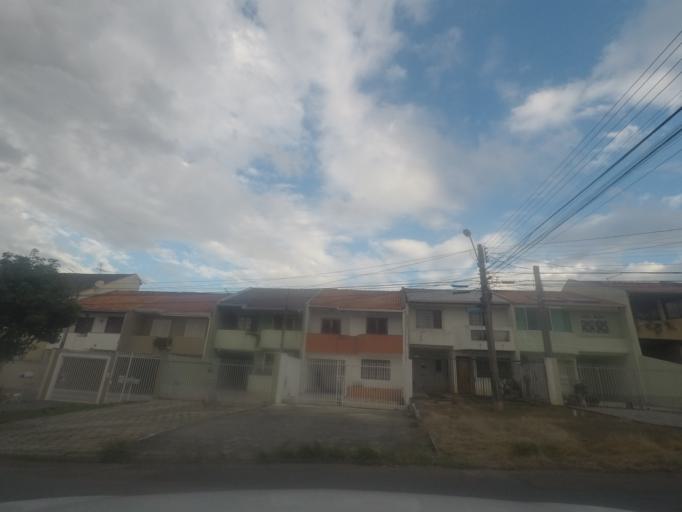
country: BR
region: Parana
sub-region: Pinhais
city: Pinhais
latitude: -25.4677
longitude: -49.2185
